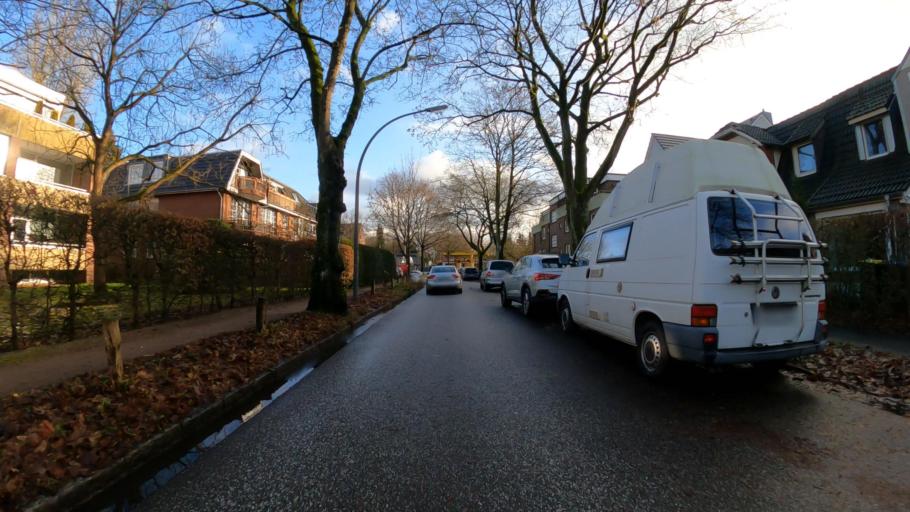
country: DE
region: Hamburg
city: Wellingsbuettel
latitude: 53.6363
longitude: 10.0907
